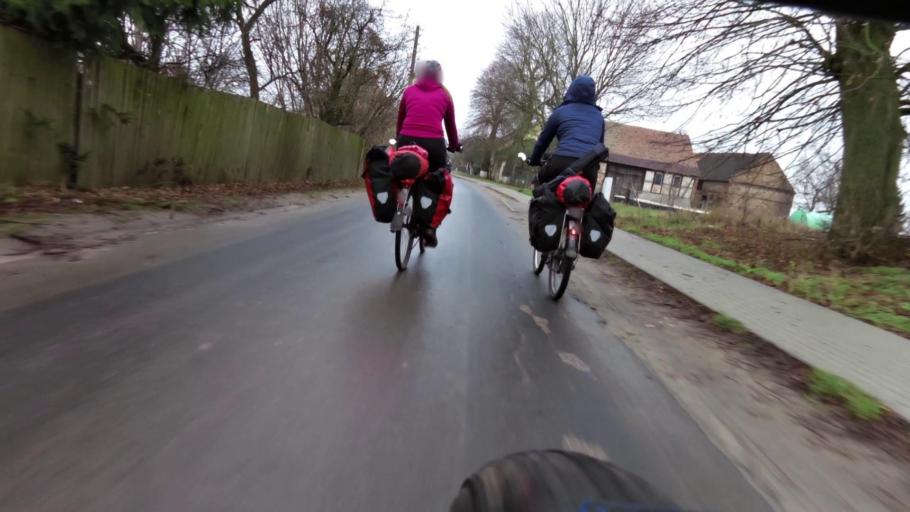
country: PL
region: West Pomeranian Voivodeship
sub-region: Powiat mysliborski
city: Debno
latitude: 52.6511
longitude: 14.7180
